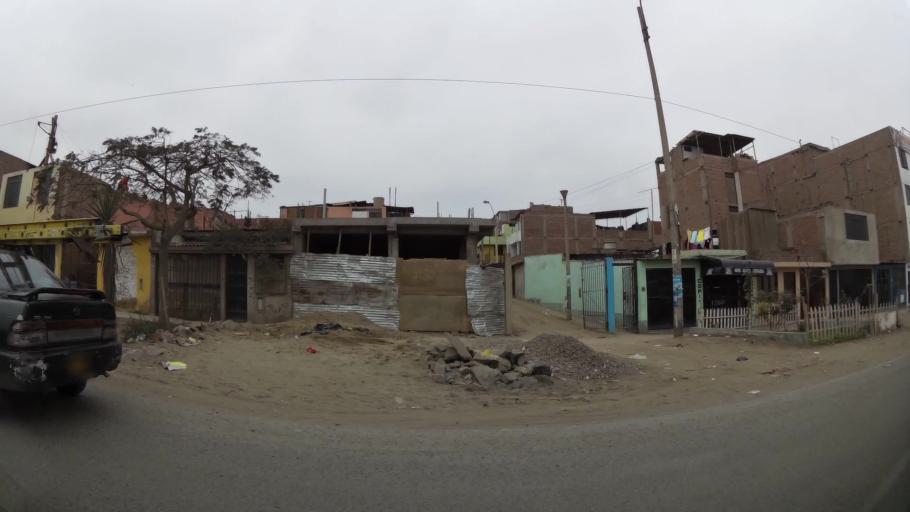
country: PE
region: Lima
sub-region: Lima
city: Surco
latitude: -12.2321
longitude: -76.9183
